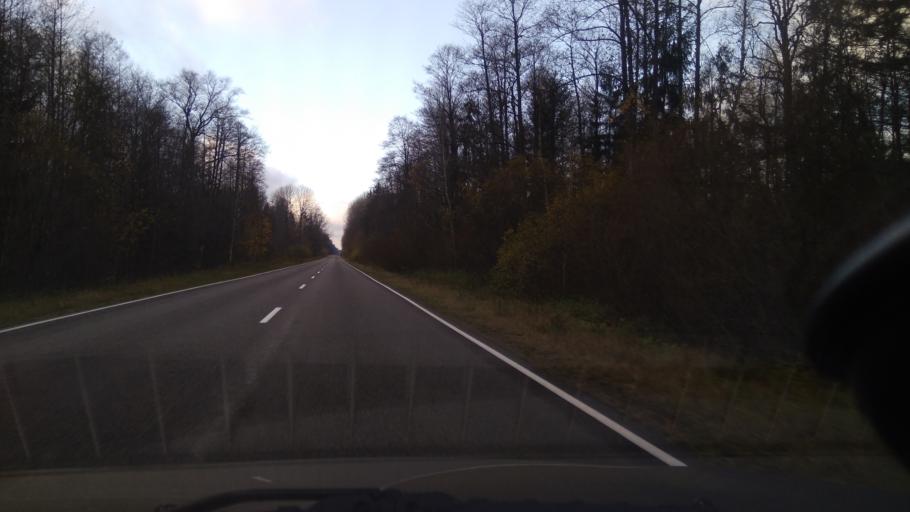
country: BY
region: Minsk
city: Urechcha
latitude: 53.2099
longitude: 27.8989
